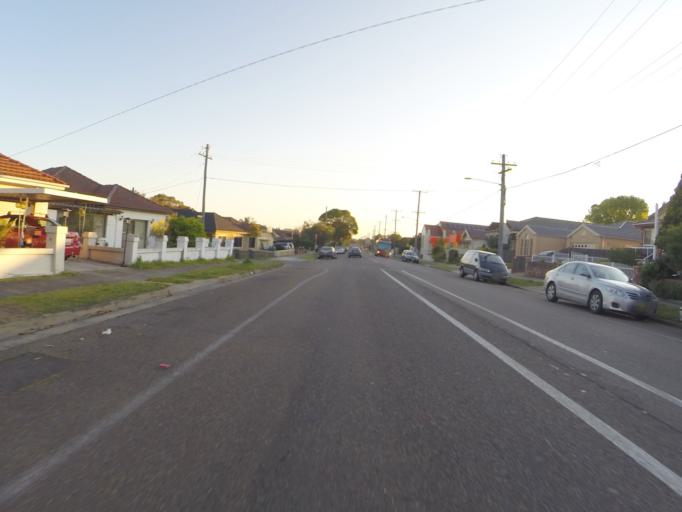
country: AU
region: New South Wales
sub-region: Rockdale
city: Bexley North
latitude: -33.9439
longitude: 151.1145
